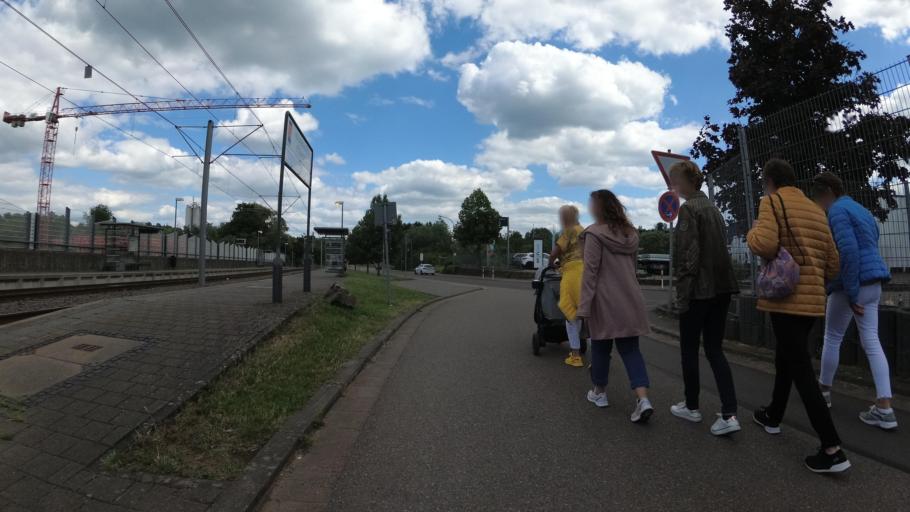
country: DE
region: Saarland
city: Riegelsberg
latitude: 49.3179
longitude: 6.9139
